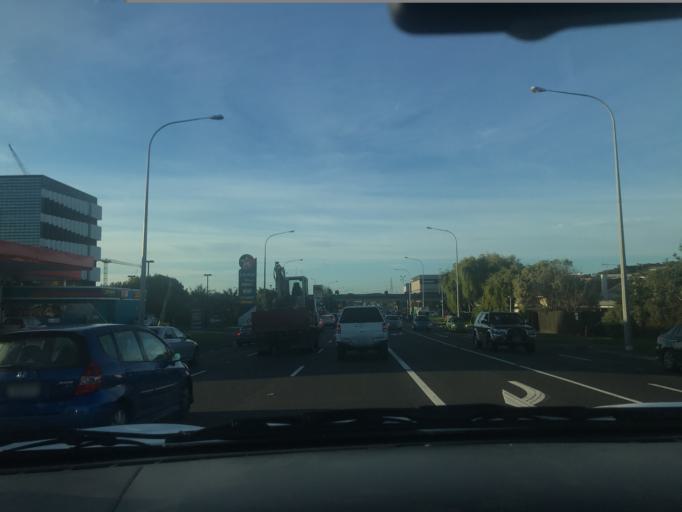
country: NZ
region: Auckland
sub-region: Auckland
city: Tamaki
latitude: -36.9135
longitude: 174.8386
